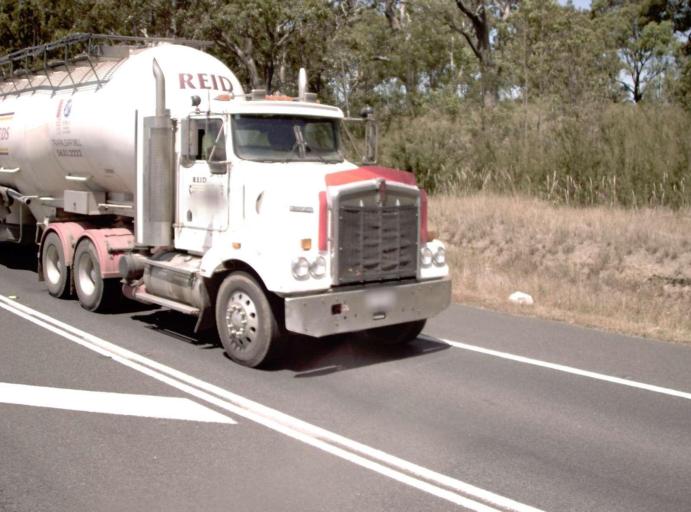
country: AU
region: Victoria
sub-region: Latrobe
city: Traralgon
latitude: -38.1693
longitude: 146.6866
